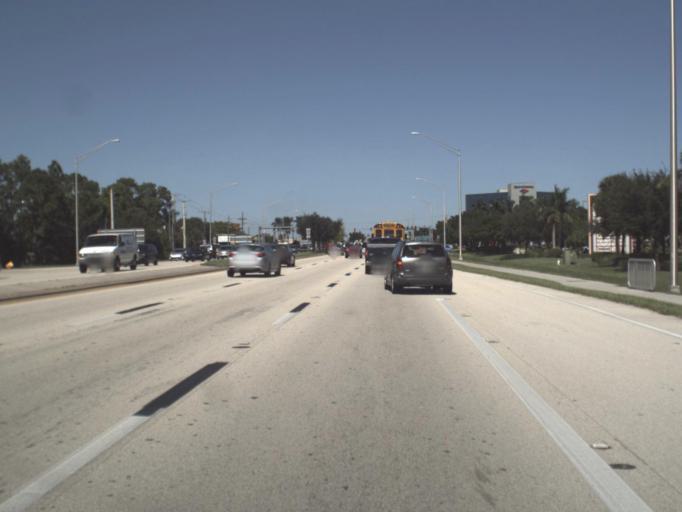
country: US
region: Florida
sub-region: Lee County
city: Villas
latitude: 26.5475
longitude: -81.8714
